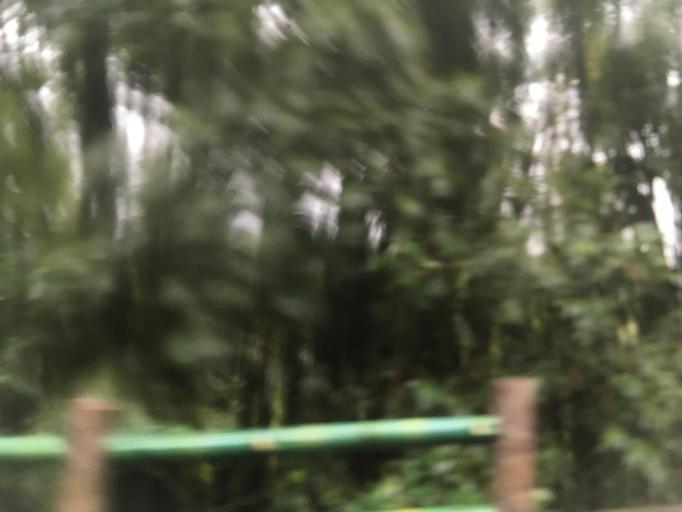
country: TW
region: Taiwan
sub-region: Keelung
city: Keelung
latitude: 25.0743
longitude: 121.9126
